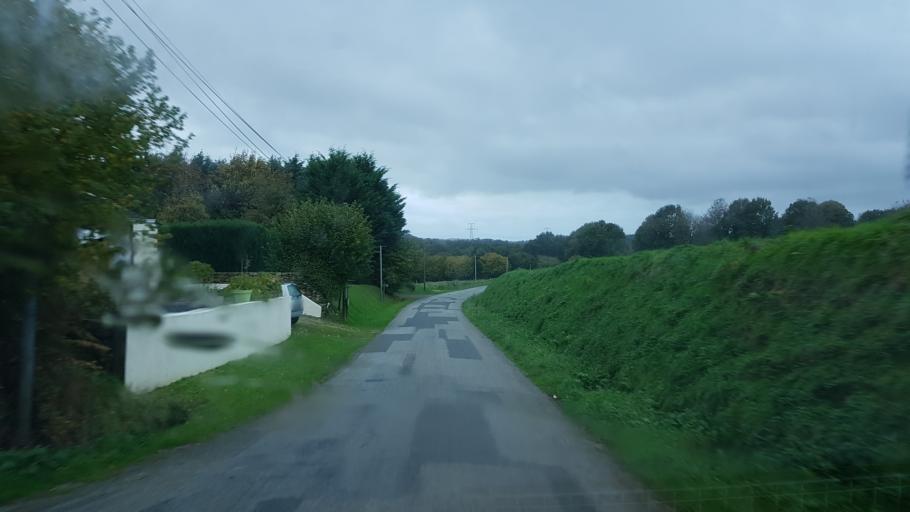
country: FR
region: Brittany
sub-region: Departement du Morbihan
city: Elven
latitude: 47.7455
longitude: -2.5576
